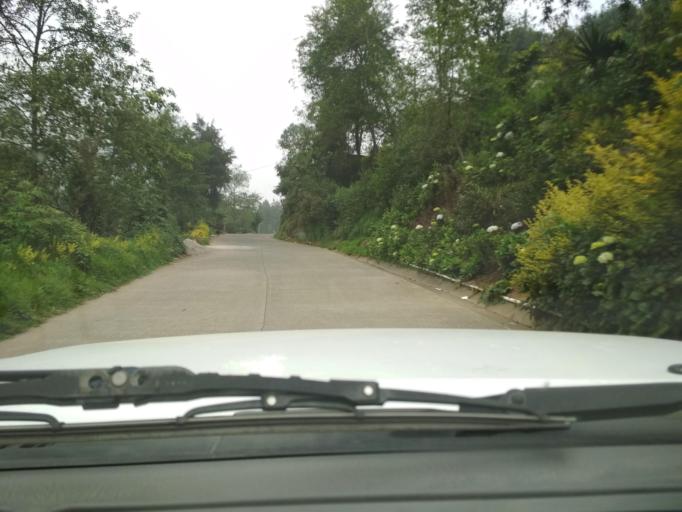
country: MX
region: Veracruz
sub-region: La Perla
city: Chilapa
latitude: 18.9747
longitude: -97.1637
